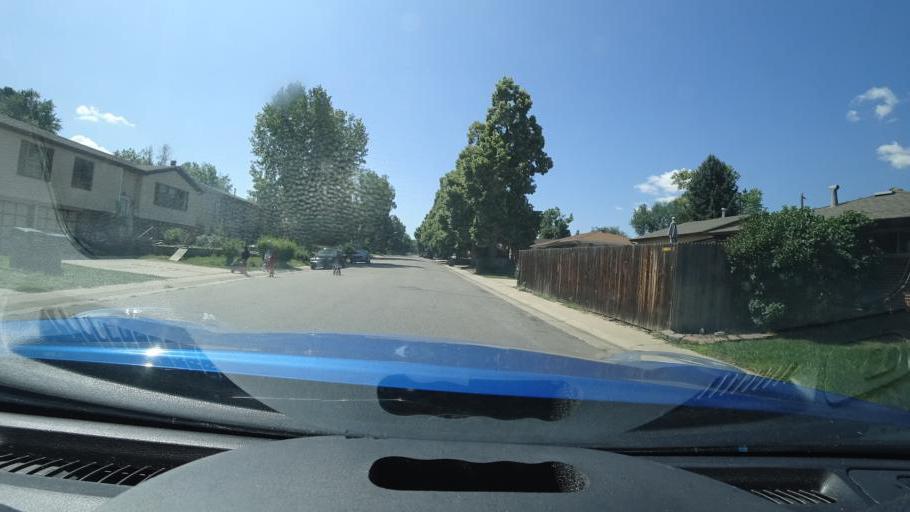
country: US
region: Colorado
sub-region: Adams County
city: Aurora
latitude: 39.7232
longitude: -104.8716
